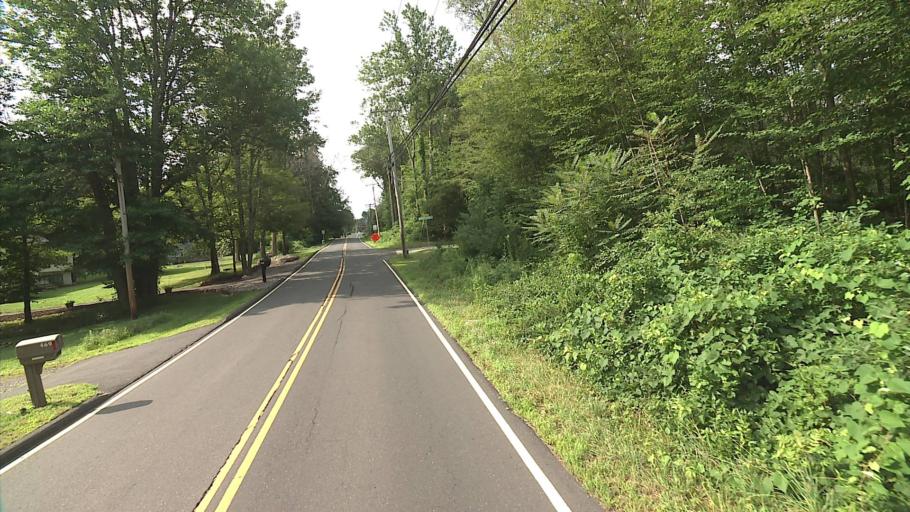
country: US
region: Connecticut
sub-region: Middlesex County
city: Moodus
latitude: 41.5493
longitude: -72.4127
